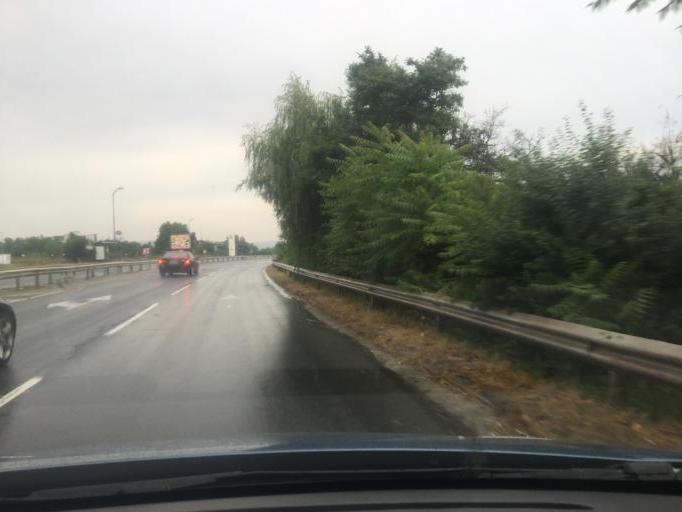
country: BG
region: Burgas
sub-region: Obshtina Burgas
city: Burgas
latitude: 42.5484
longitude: 27.4749
